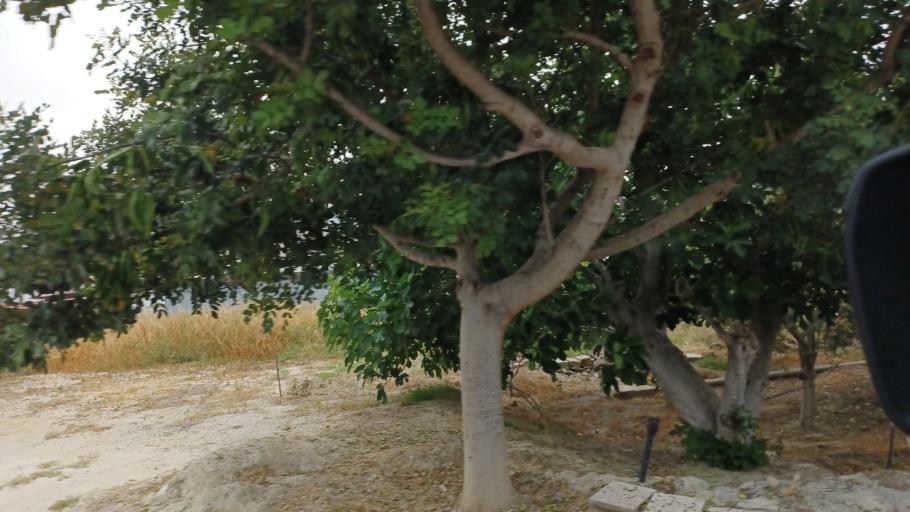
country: CY
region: Lefkosia
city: Mammari
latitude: 35.1744
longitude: 33.2035
